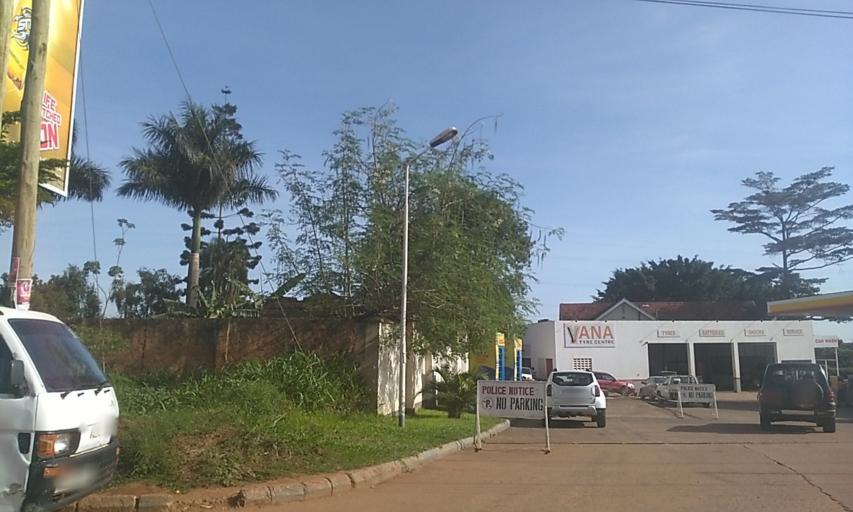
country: UG
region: Central Region
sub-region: Wakiso District
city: Kireka
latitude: 0.3532
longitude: 32.6103
